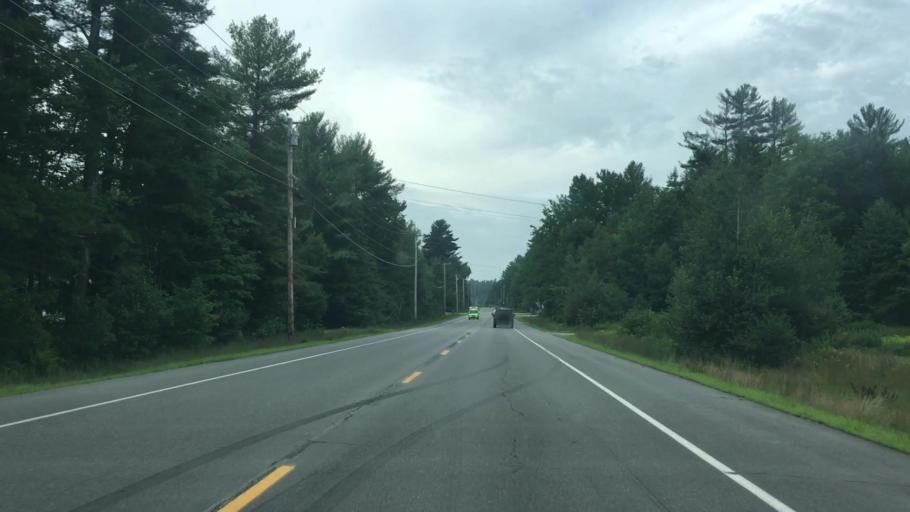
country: US
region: Maine
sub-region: York County
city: Lebanon
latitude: 43.4058
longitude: -70.8726
